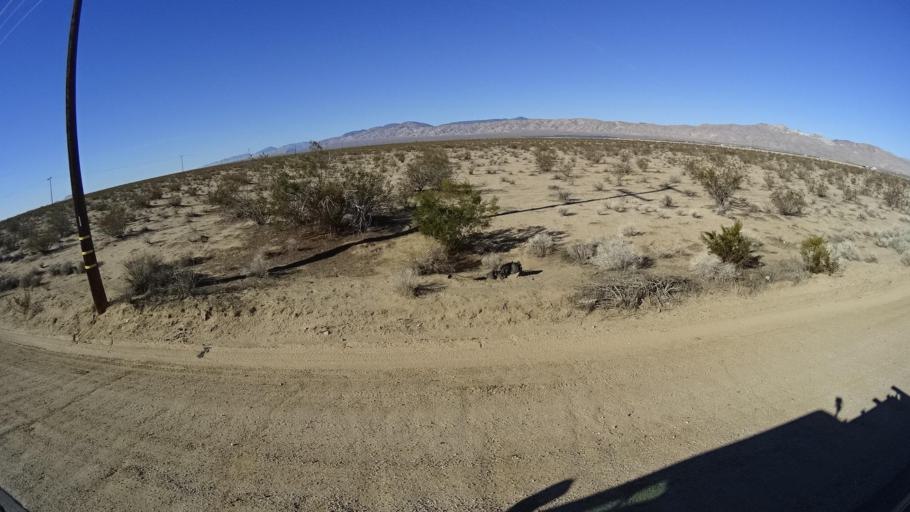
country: US
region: California
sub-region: Kern County
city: California City
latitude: 35.1856
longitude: -117.9858
